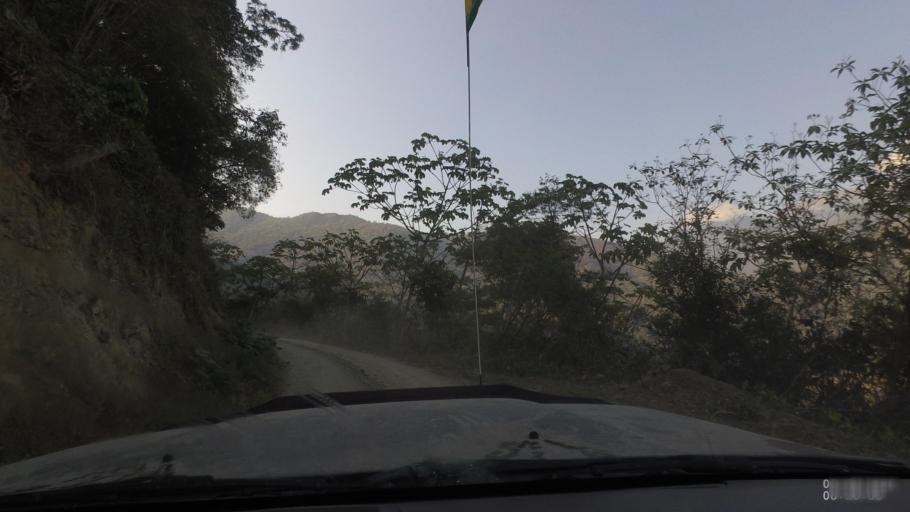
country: BO
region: La Paz
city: Quime
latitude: -16.5008
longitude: -66.7679
